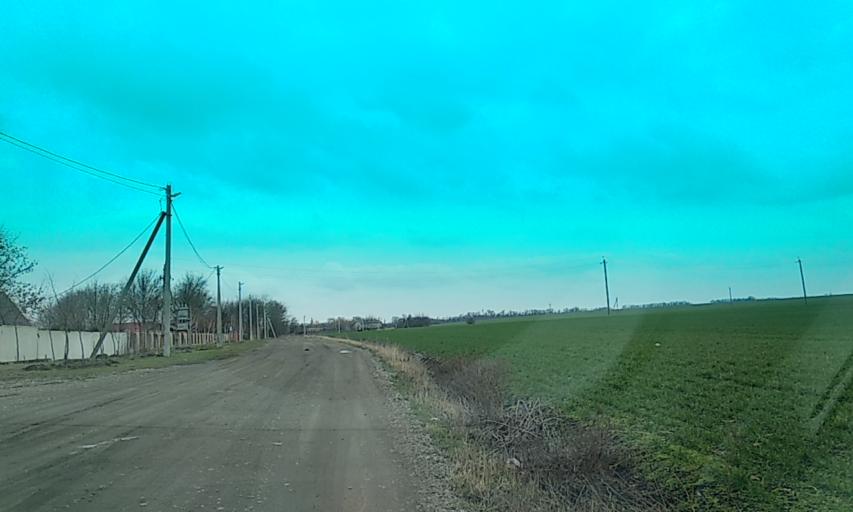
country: RU
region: Krasnodarskiy
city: Vyselki
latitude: 45.6614
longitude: 39.7037
